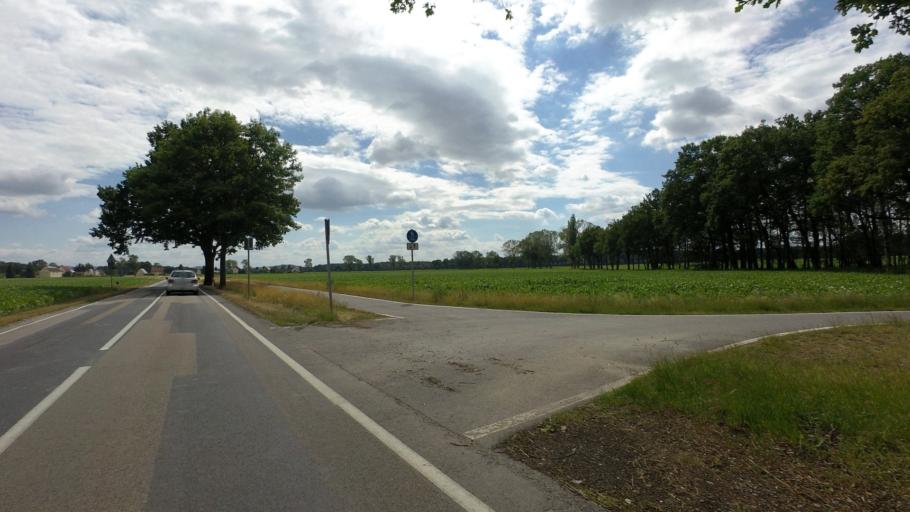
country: DE
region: Saxony
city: Ossling
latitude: 51.3333
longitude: 14.1568
